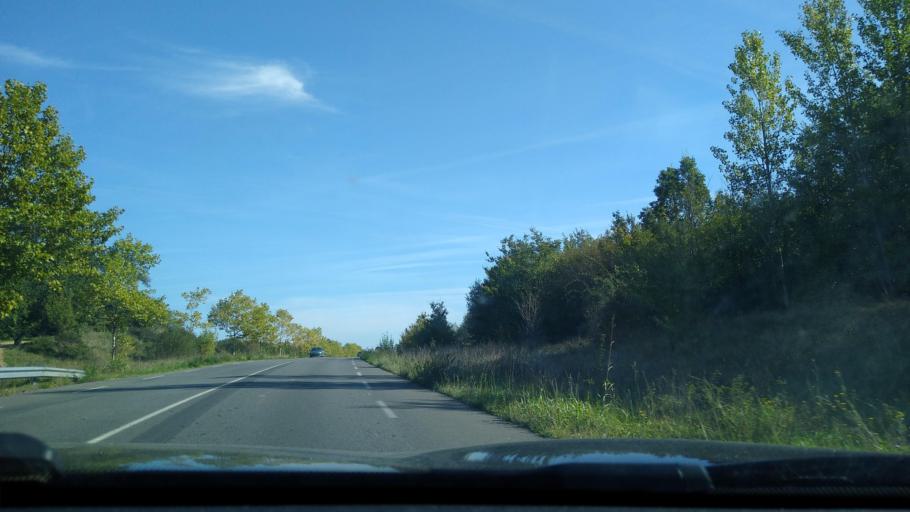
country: FR
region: Midi-Pyrenees
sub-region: Departement de la Haute-Garonne
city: Mondonville
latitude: 43.6713
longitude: 1.2968
